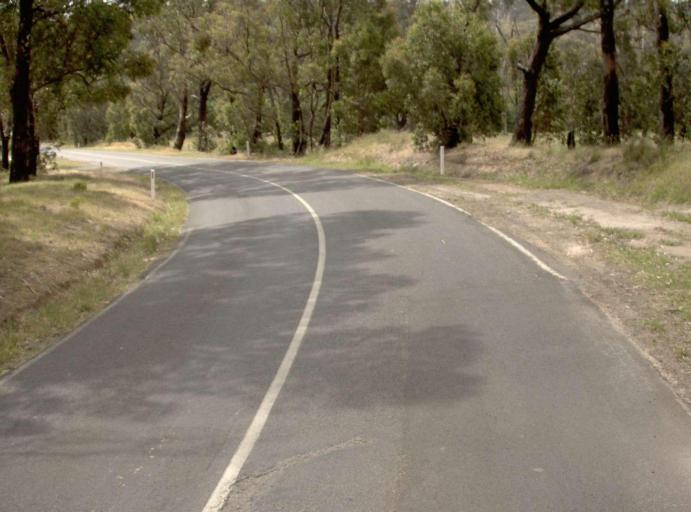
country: AU
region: Victoria
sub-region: Latrobe
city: Traralgon
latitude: -38.3175
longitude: 146.5735
